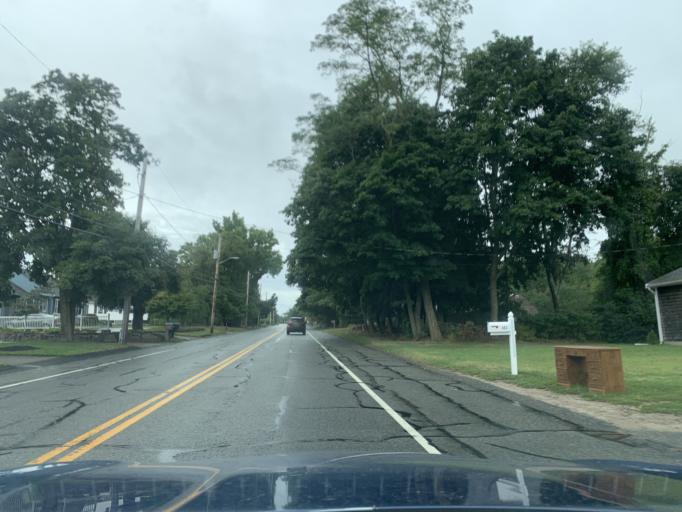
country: US
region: Rhode Island
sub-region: Bristol County
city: Warren
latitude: 41.7600
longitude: -71.2698
